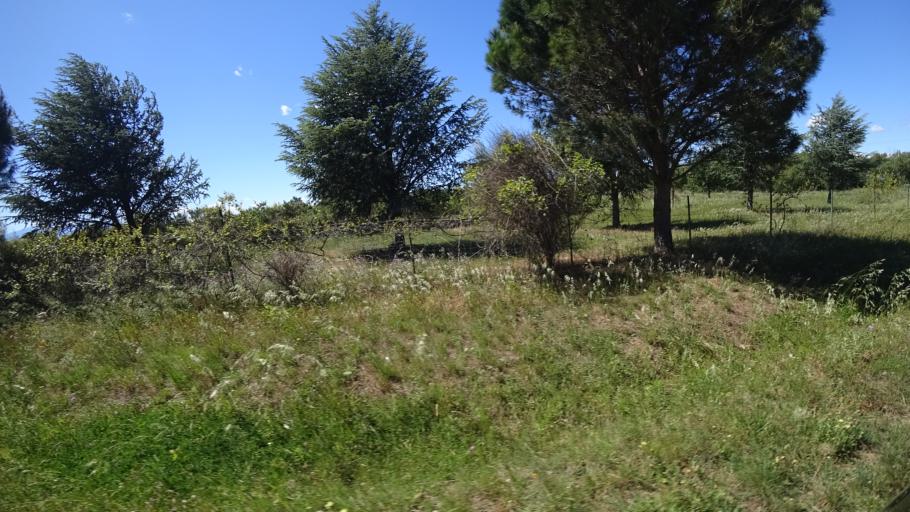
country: FR
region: Languedoc-Roussillon
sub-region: Departement des Pyrenees-Orientales
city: Saleilles
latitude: 42.6613
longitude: 2.9632
